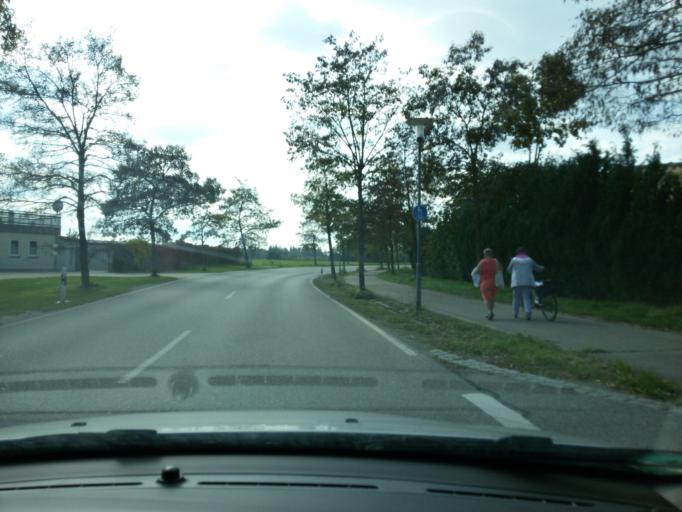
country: DE
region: Bavaria
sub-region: Upper Bavaria
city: Kaufering
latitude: 48.0792
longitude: 10.8512
